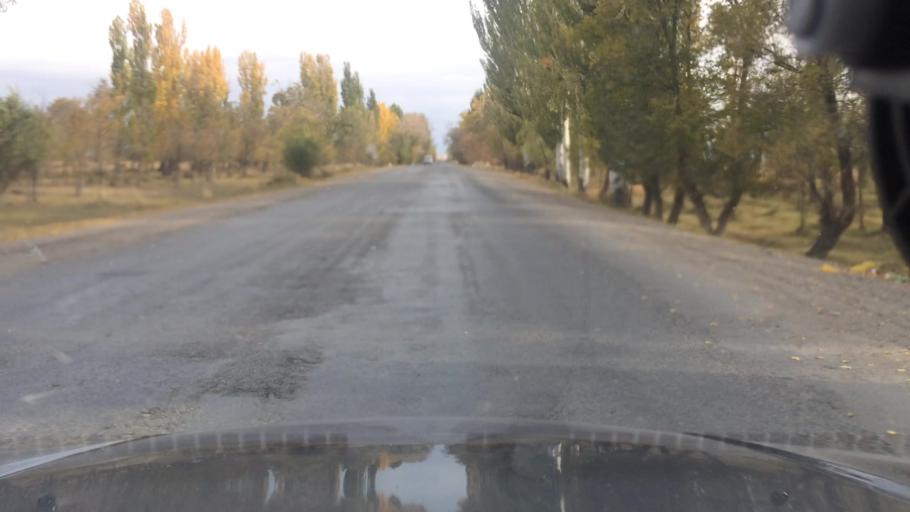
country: KG
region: Ysyk-Koel
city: Karakol
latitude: 42.5412
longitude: 78.3848
